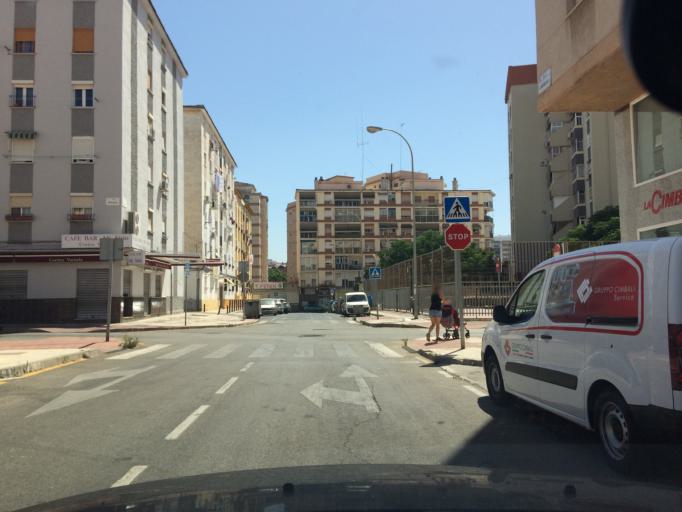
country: ES
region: Andalusia
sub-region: Provincia de Malaga
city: Malaga
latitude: 36.7089
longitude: -4.4479
